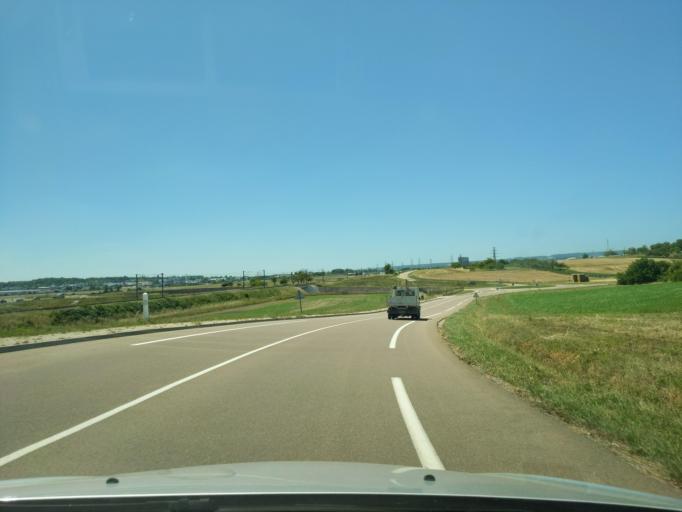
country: FR
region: Bourgogne
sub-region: Departement de la Cote-d'Or
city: Ruffey-les-Echirey
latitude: 47.3684
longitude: 5.0734
